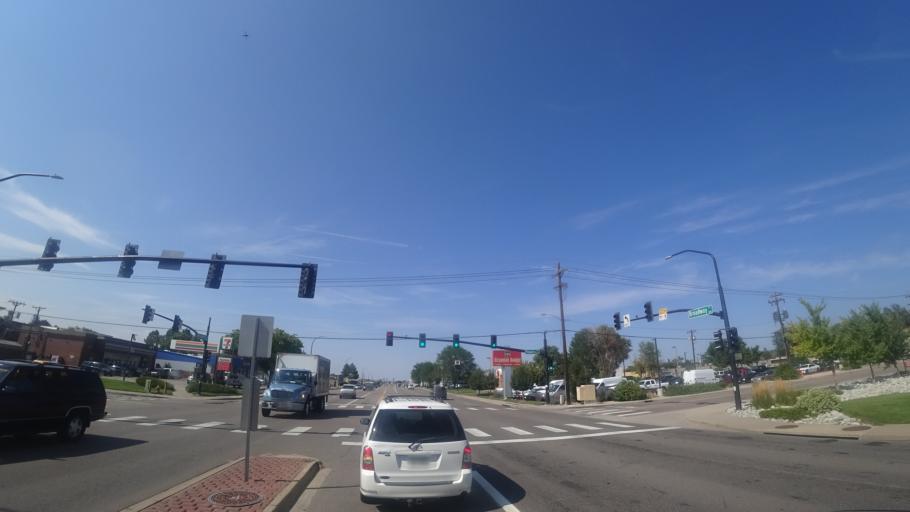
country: US
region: Colorado
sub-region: Arapahoe County
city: Littleton
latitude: 39.6148
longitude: -104.9880
